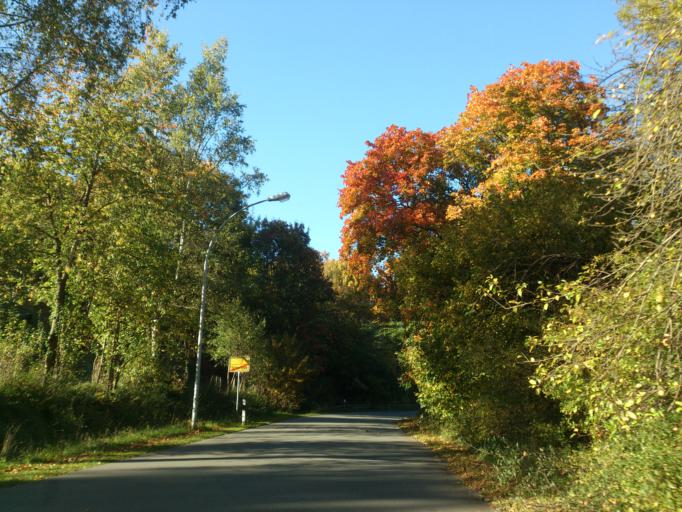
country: DE
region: North Rhine-Westphalia
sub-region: Regierungsbezirk Detmold
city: Willebadessen
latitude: 51.5343
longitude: 9.0317
